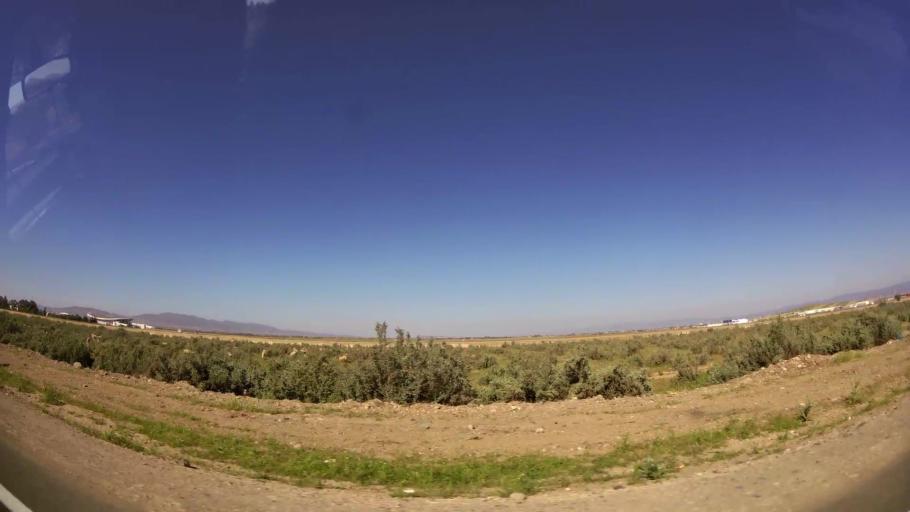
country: MA
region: Oriental
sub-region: Oujda-Angad
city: Oujda
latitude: 34.7768
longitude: -1.9451
